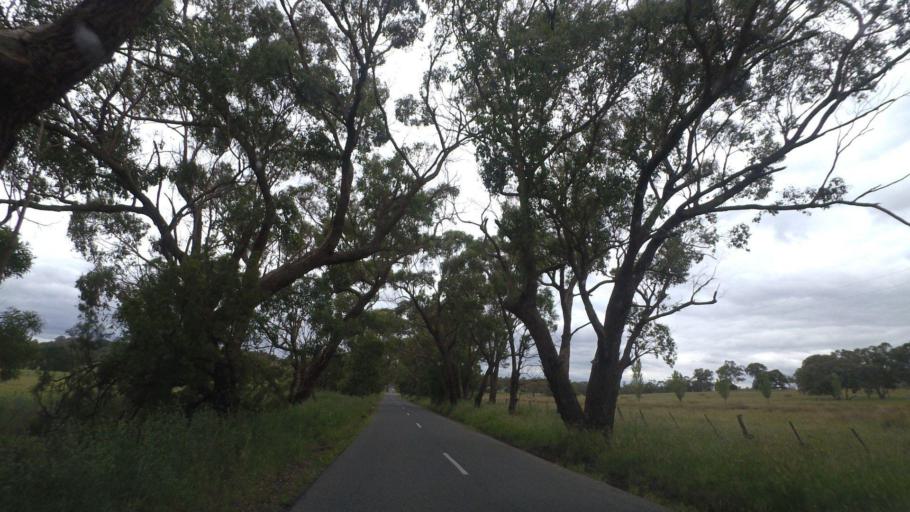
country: AU
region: Victoria
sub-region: Yarra Ranges
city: Mount Evelyn
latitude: -37.7385
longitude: 145.4076
